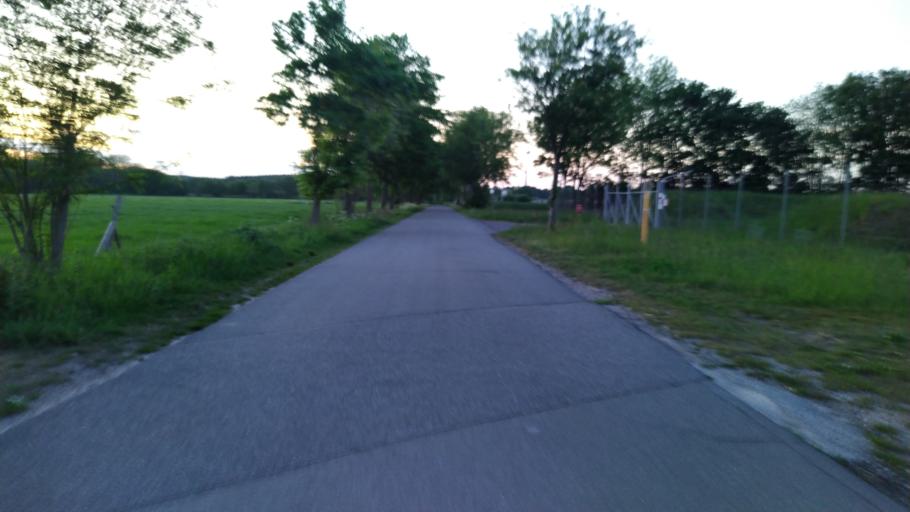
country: DE
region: Lower Saxony
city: Bargstedt
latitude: 53.4730
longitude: 9.4707
